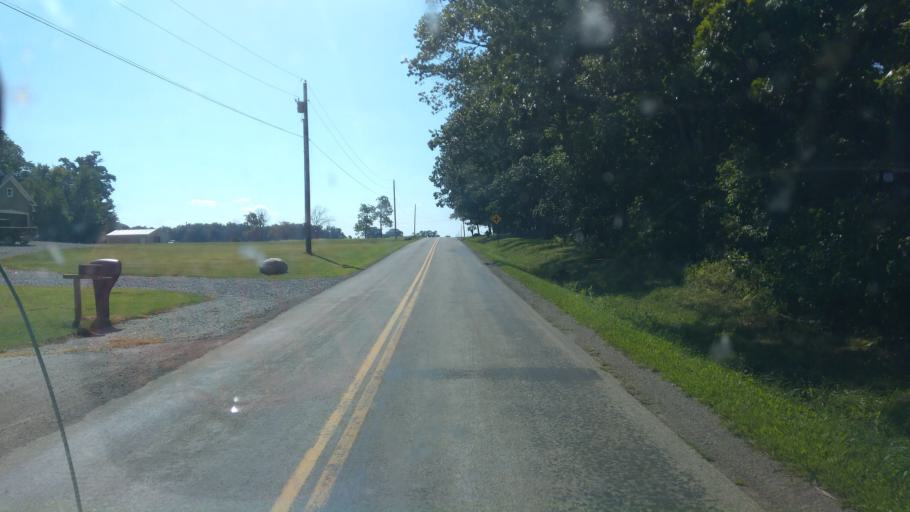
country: US
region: Ohio
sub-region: Ashland County
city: Ashland
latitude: 40.9707
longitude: -82.3277
